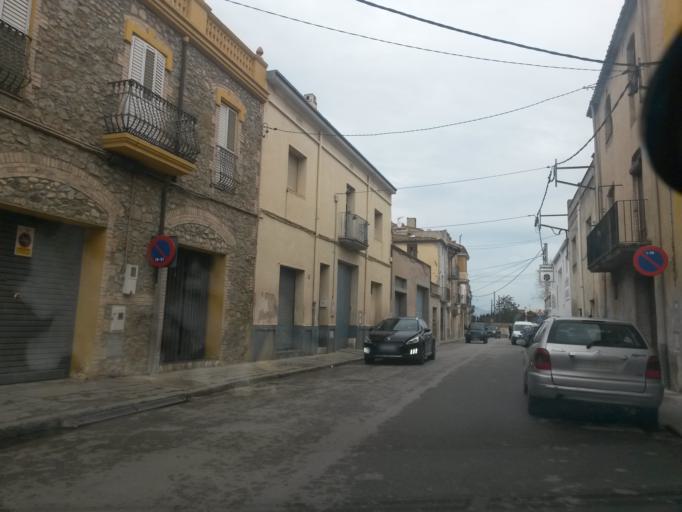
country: ES
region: Catalonia
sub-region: Provincia de Girona
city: Cabanes
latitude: 42.3081
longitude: 2.9765
